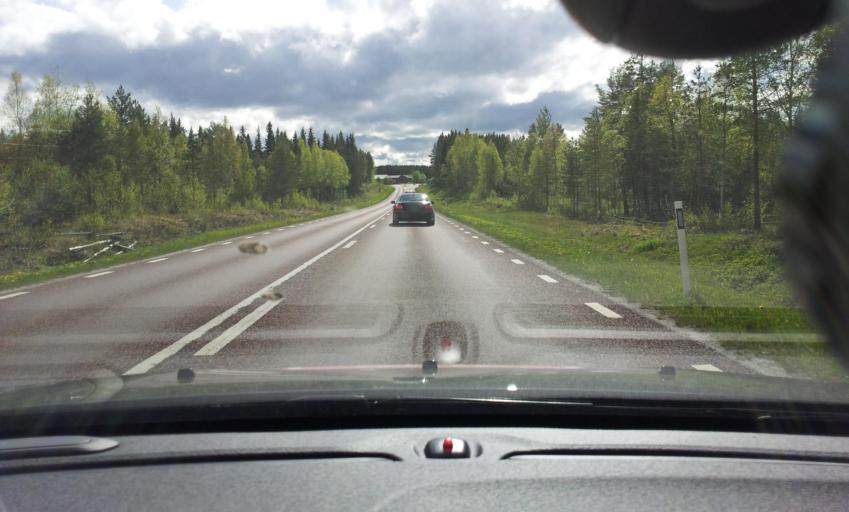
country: SE
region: Jaemtland
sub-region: OEstersunds Kommun
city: Brunflo
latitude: 63.0204
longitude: 14.7421
